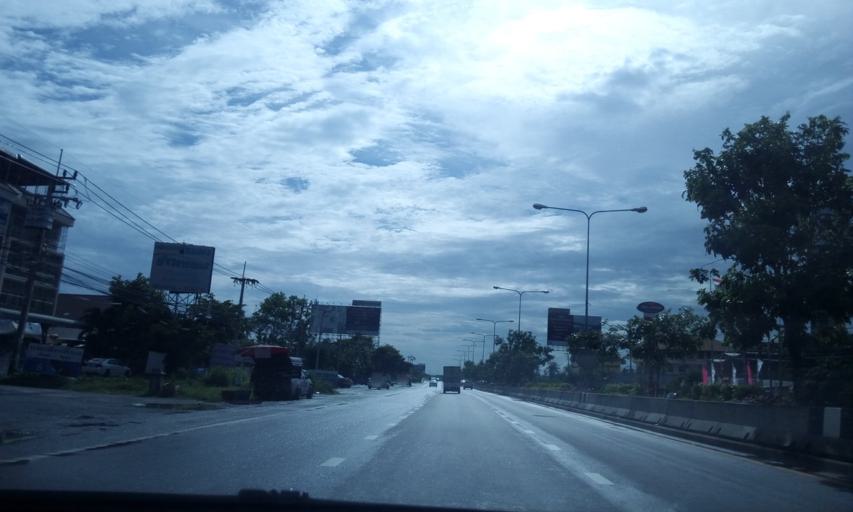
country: TH
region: Nonthaburi
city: Pak Kret
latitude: 13.9237
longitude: 100.4732
